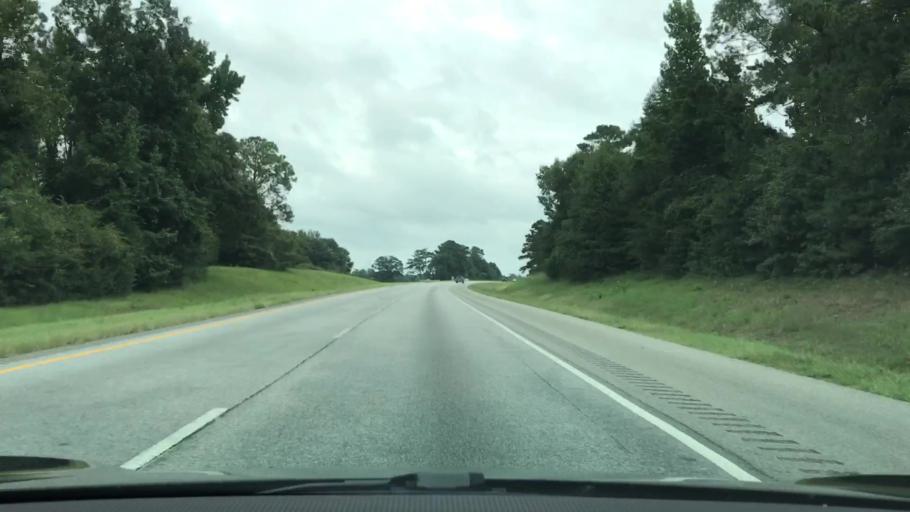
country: US
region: Alabama
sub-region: Lee County
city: Auburn
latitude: 32.5253
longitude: -85.5701
